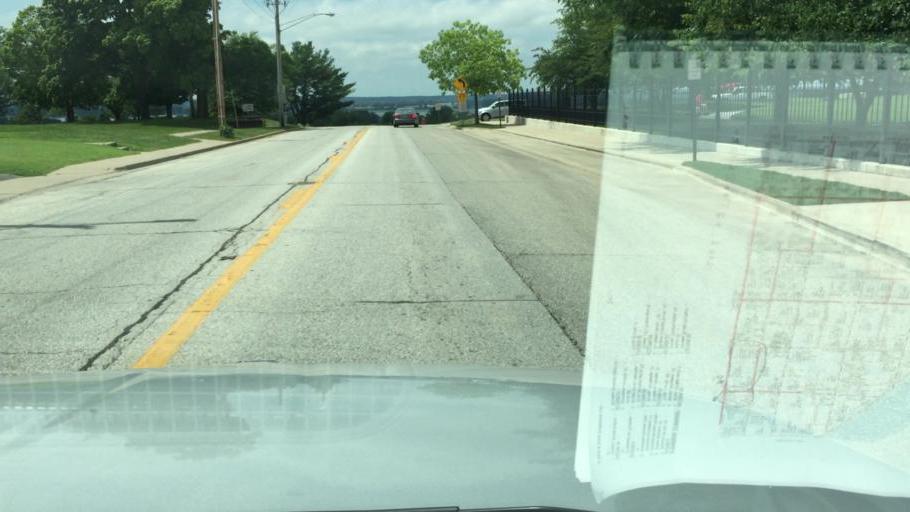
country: US
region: Illinois
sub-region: Hancock County
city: Nauvoo
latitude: 40.5498
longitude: -91.3841
